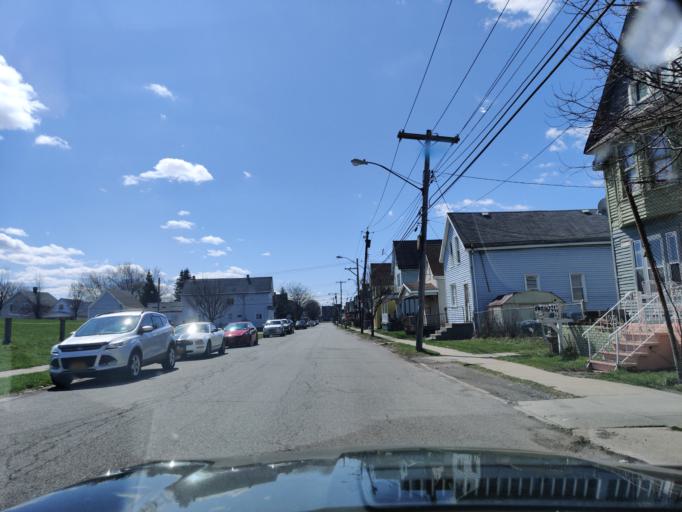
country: US
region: New York
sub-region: Erie County
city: Sloan
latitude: 42.8805
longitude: -78.8332
